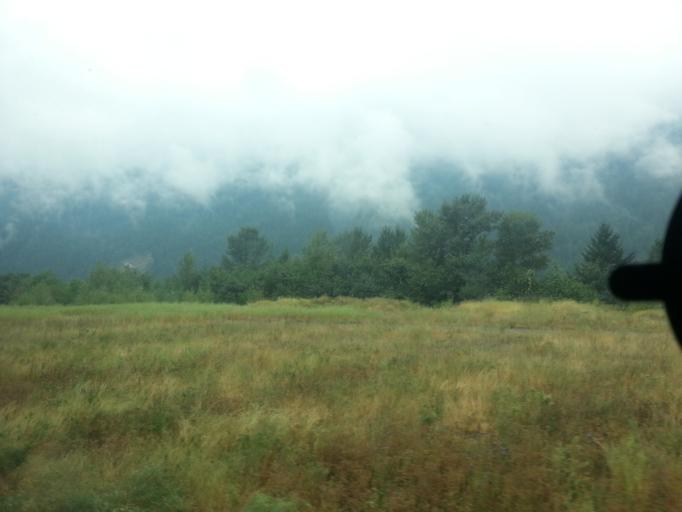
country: CA
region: British Columbia
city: Hope
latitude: 49.8480
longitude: -121.4344
